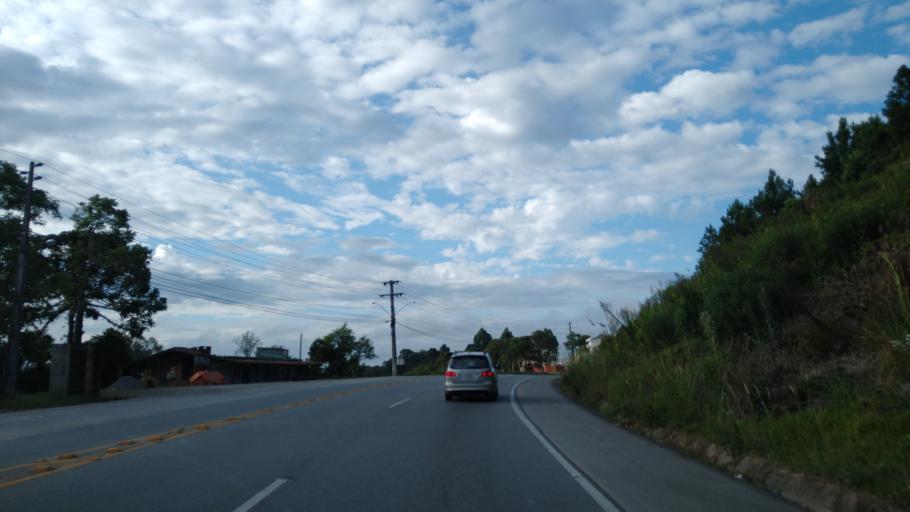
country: BR
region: Santa Catarina
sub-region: Sao Bento Do Sul
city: Sao Bento do Sul
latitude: -26.2346
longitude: -49.4258
